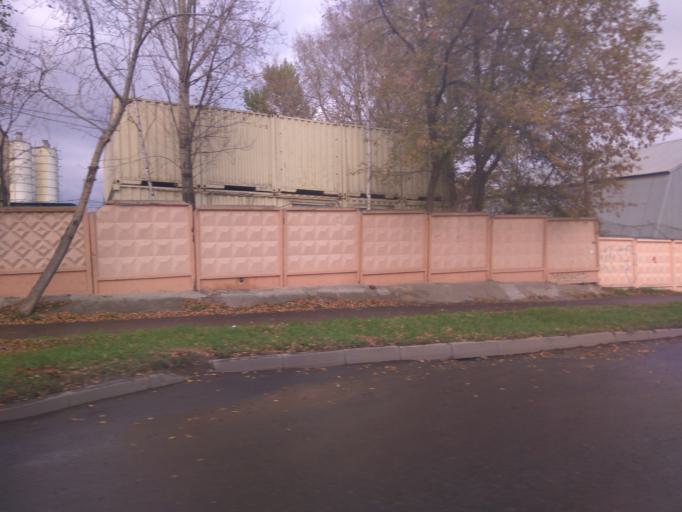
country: RU
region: Moscow
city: Tsaritsyno
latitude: 55.6339
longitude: 37.6403
